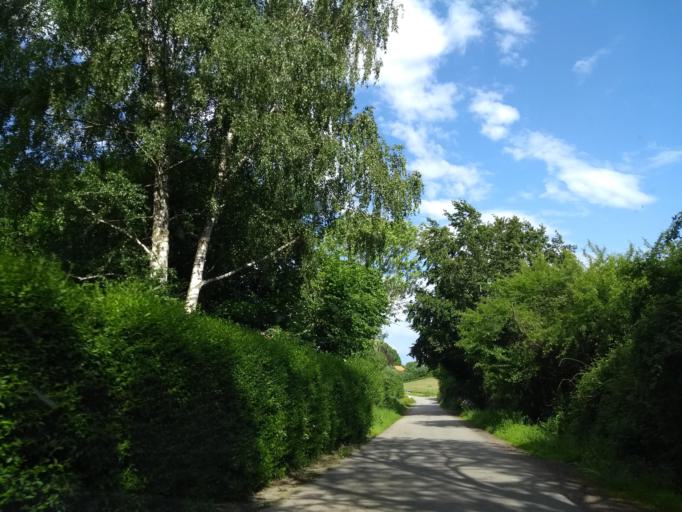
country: DE
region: Schleswig-Holstein
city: Thumby
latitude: 54.5540
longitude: 9.9322
